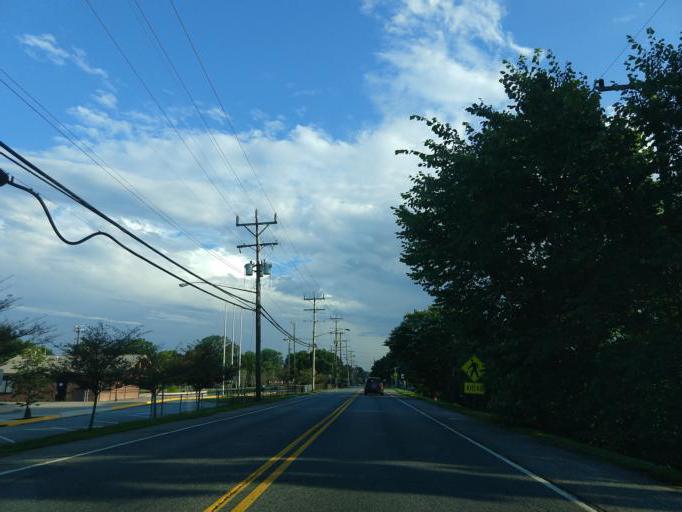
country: US
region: Maryland
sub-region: Prince George's County
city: Berwyn Heights
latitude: 39.0038
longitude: -76.9241
